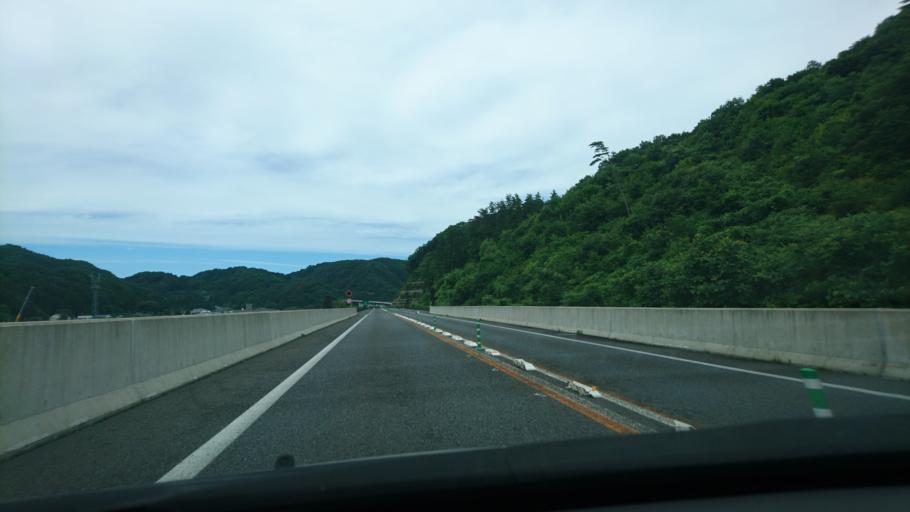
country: JP
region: Iwate
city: Miyako
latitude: 39.9974
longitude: 141.8850
